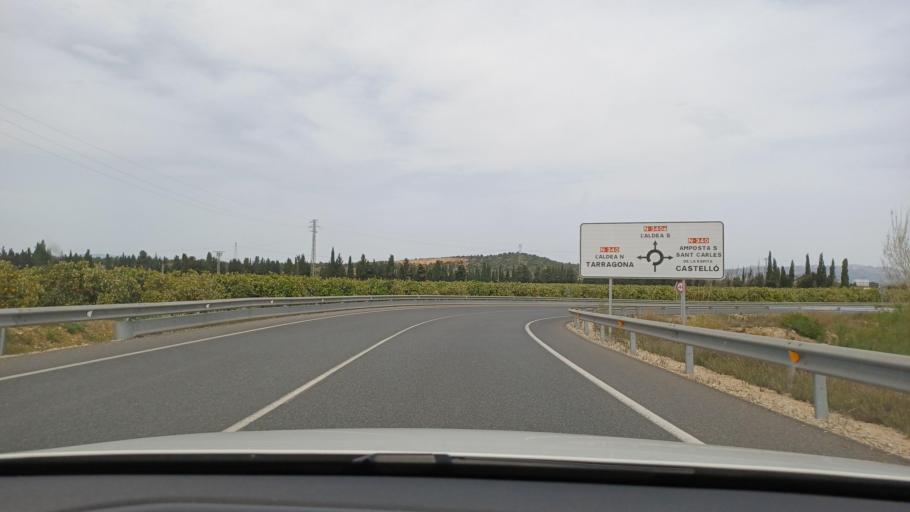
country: ES
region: Catalonia
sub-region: Provincia de Tarragona
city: Amposta
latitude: 40.7285
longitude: 0.5900
